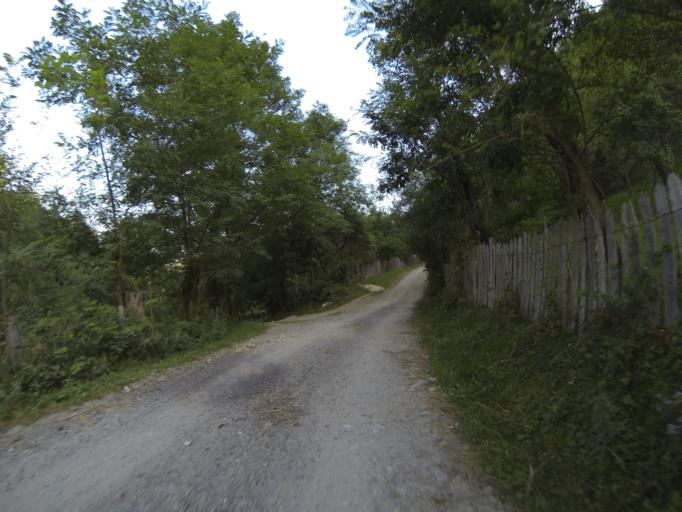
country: RO
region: Valcea
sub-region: Comuna Horezu
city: Horezu
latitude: 45.1832
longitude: 23.9918
